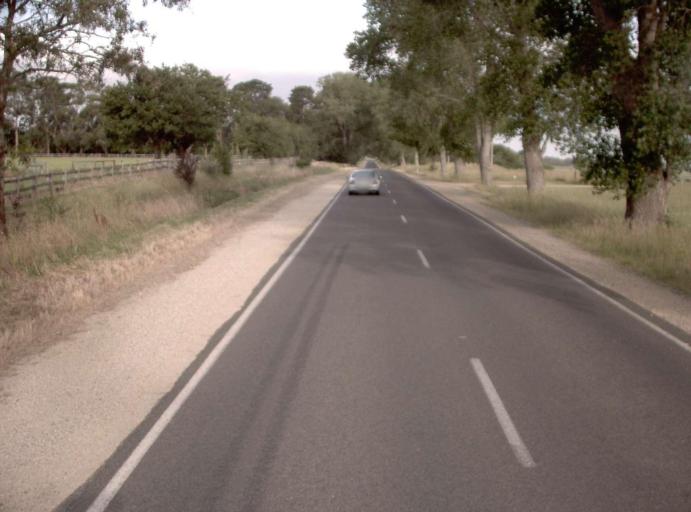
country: AU
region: Victoria
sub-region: Wellington
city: Heyfield
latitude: -37.9682
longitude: 146.9402
